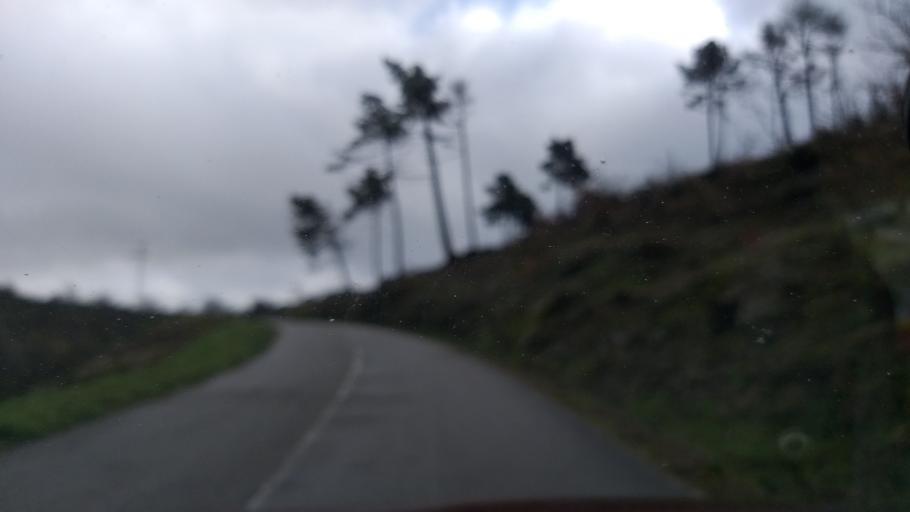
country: PT
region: Guarda
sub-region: Celorico da Beira
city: Celorico da Beira
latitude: 40.7126
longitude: -7.4194
